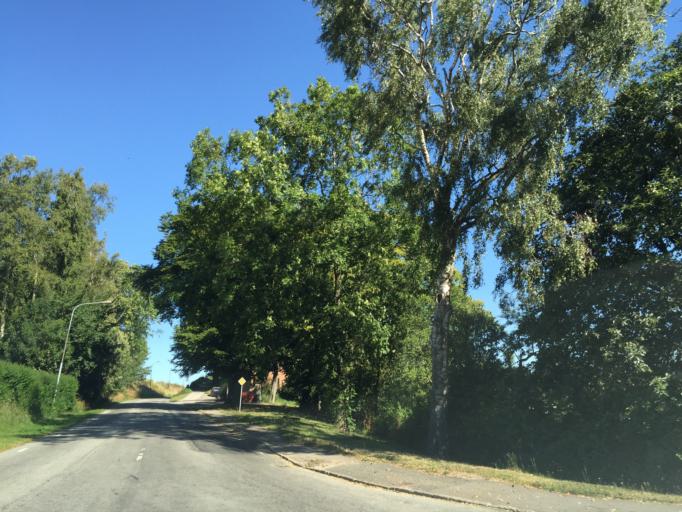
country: SE
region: Skane
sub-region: Ystads Kommun
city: Kopingebro
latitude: 55.4437
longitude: 14.1218
